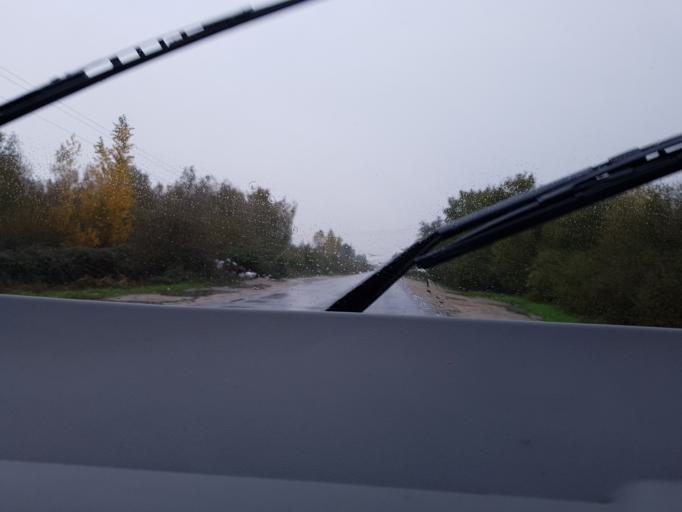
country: FR
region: Aquitaine
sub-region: Departement de la Gironde
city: Saint-Louis-de-Montferrand
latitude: 44.9453
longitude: -0.5212
